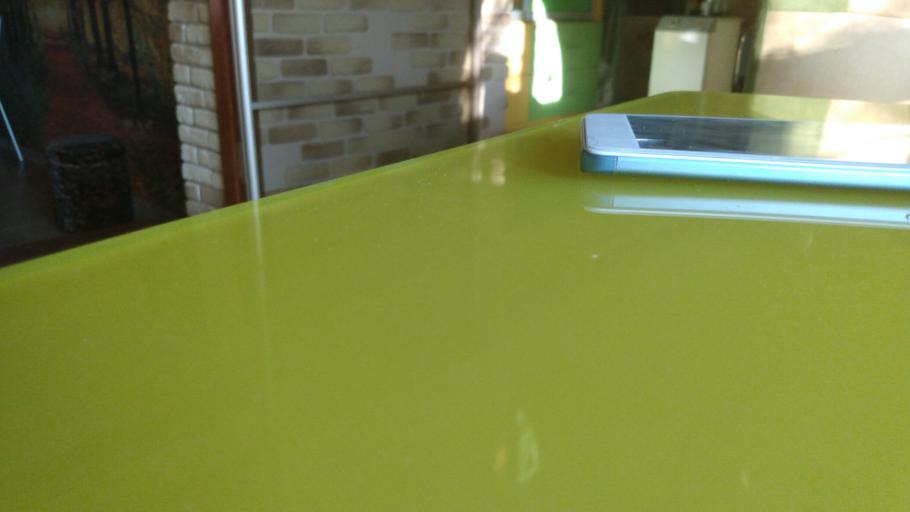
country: RU
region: Tverskaya
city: Vyshniy Volochek
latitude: 57.4513
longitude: 34.5726
